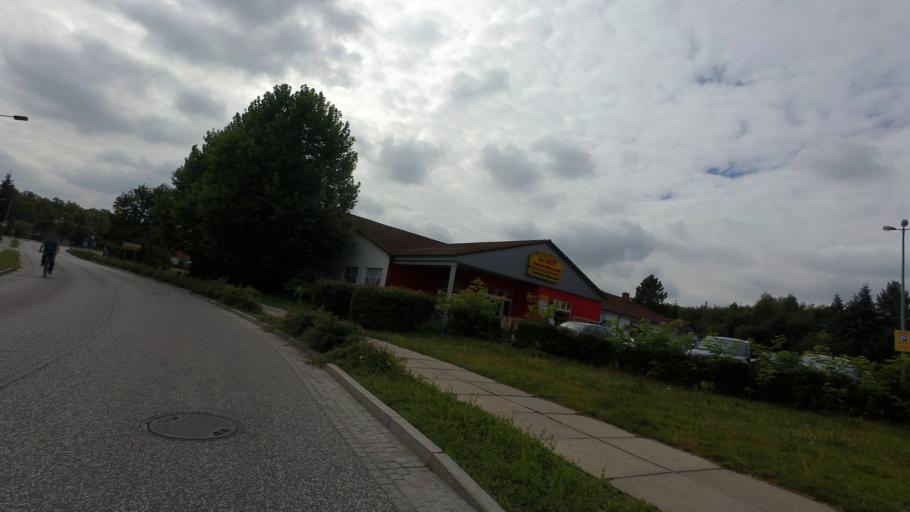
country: DE
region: Brandenburg
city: Luckau
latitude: 51.8520
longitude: 13.7028
